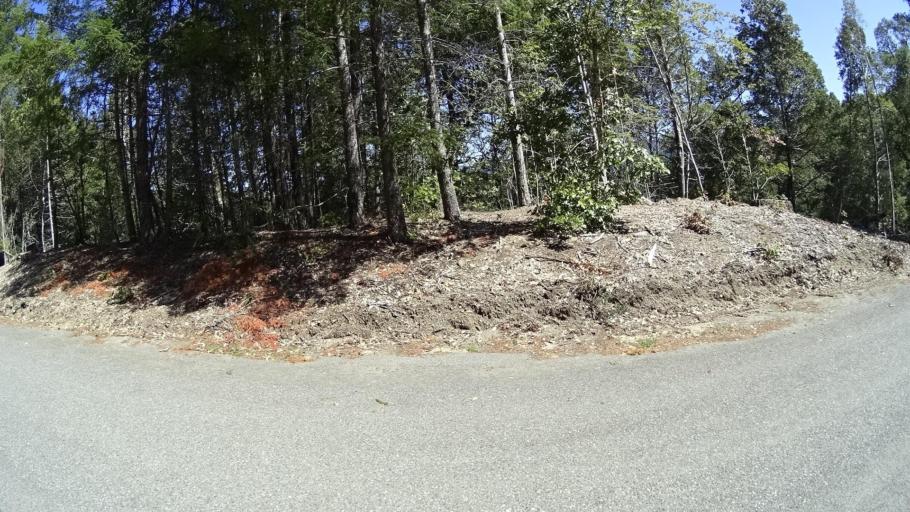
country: US
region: California
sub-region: Humboldt County
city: Redway
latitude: 40.1536
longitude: -124.0691
